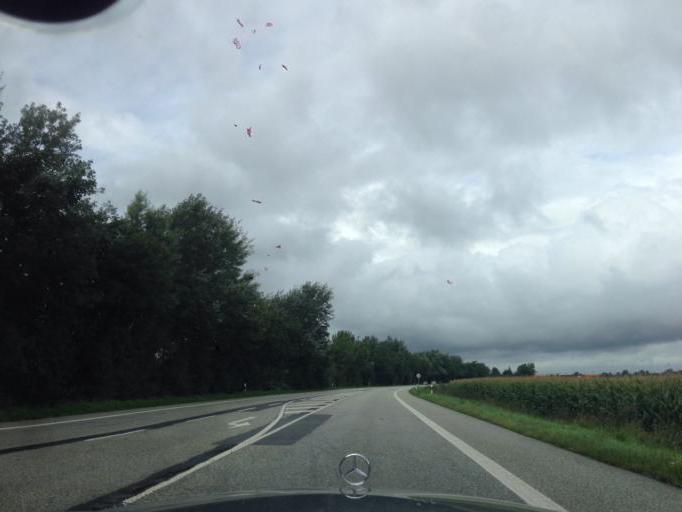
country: DE
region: Schleswig-Holstein
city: Risum-Lindholm
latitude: 54.7723
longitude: 8.8590
